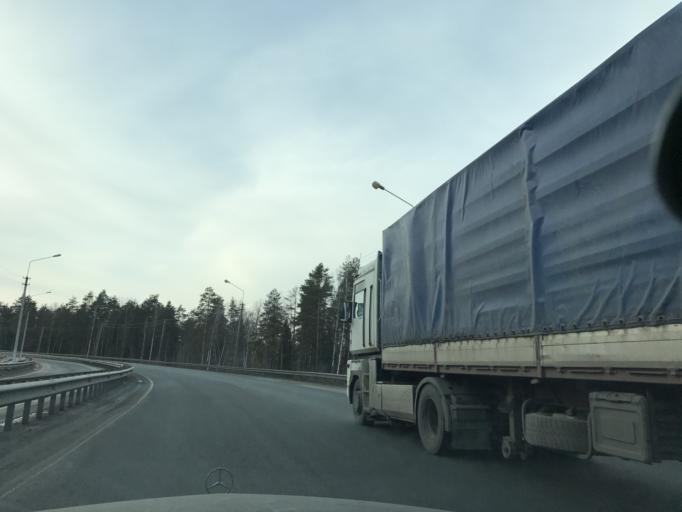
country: RU
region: Vladimir
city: Kameshkovo
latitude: 56.1967
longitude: 40.9600
